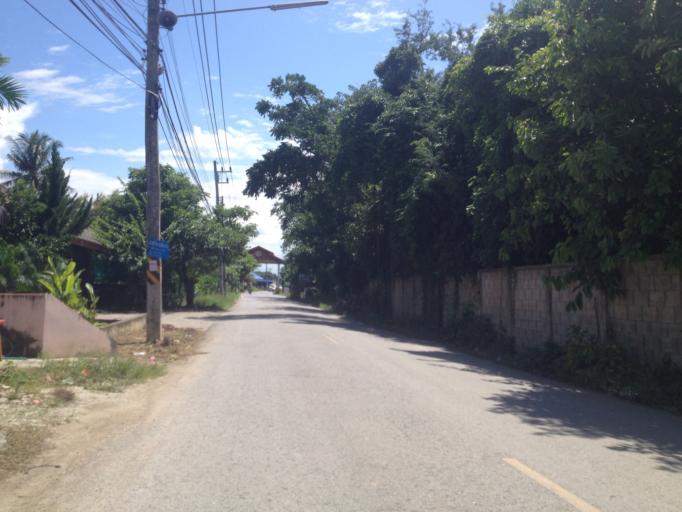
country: TH
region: Chiang Mai
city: Hang Dong
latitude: 18.6616
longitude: 98.9212
